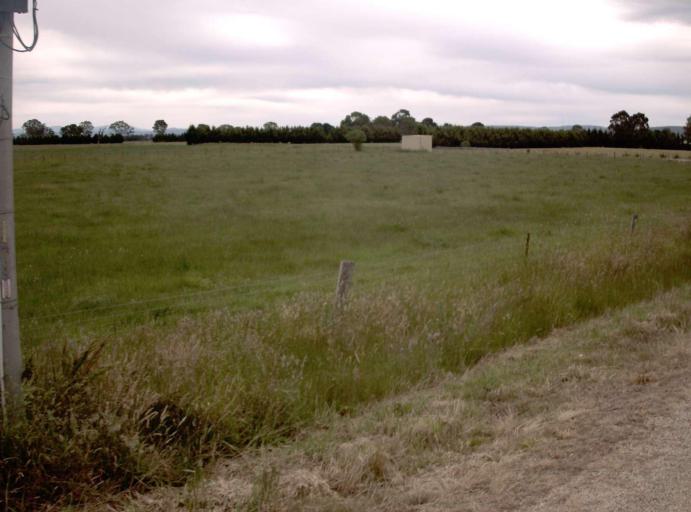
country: AU
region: Victoria
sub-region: East Gippsland
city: Bairnsdale
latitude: -37.8693
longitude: 147.5615
